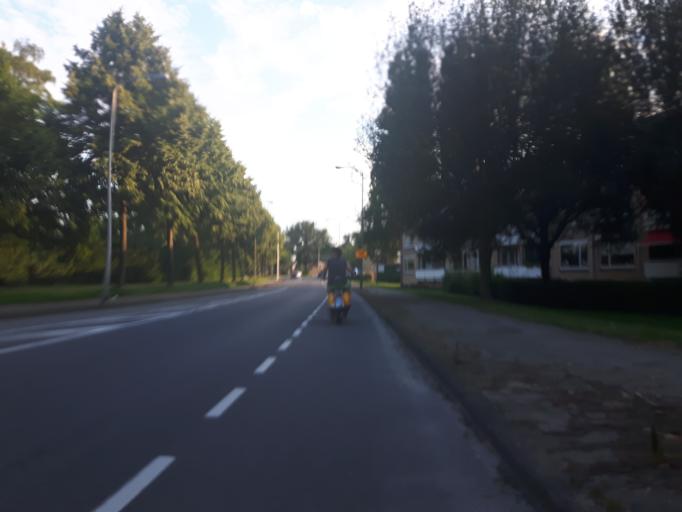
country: NL
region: Overijssel
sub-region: Gemeente Hengelo
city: Hengelo
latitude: 52.2523
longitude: 6.8043
